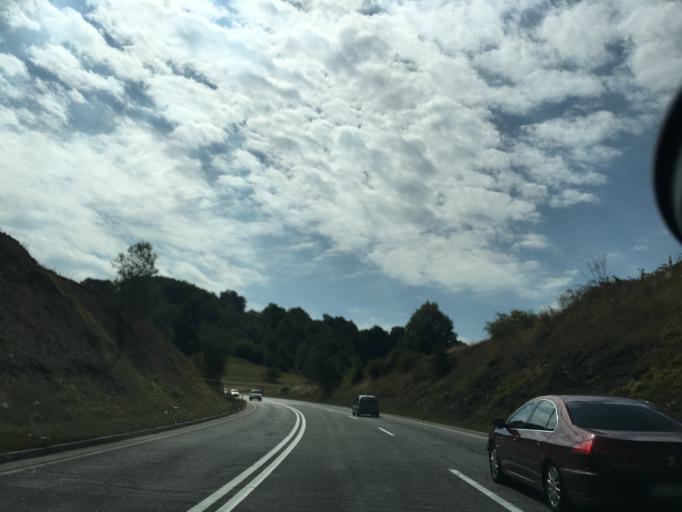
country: RS
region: Central Serbia
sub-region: Zlatiborski Okrug
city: Cajetina
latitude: 43.7438
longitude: 19.7087
